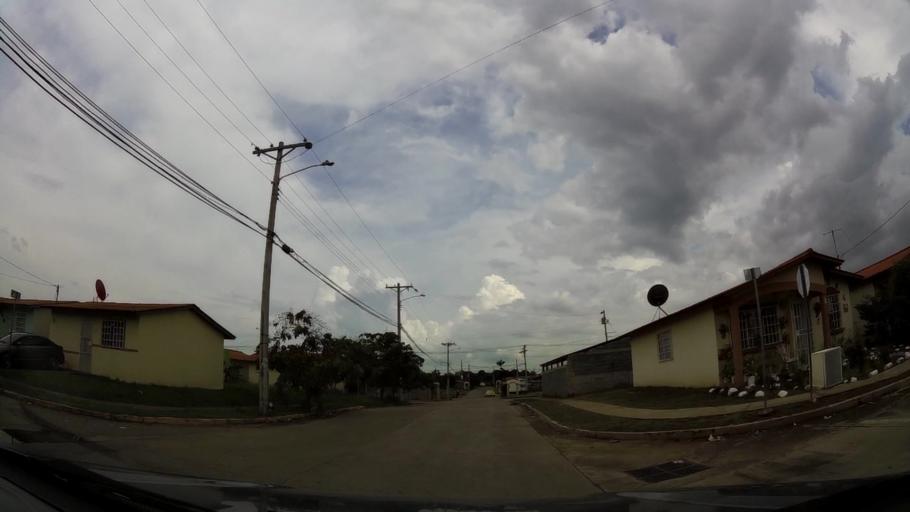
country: PA
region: Panama
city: Cabra Numero Uno
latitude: 9.1156
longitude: -79.3209
